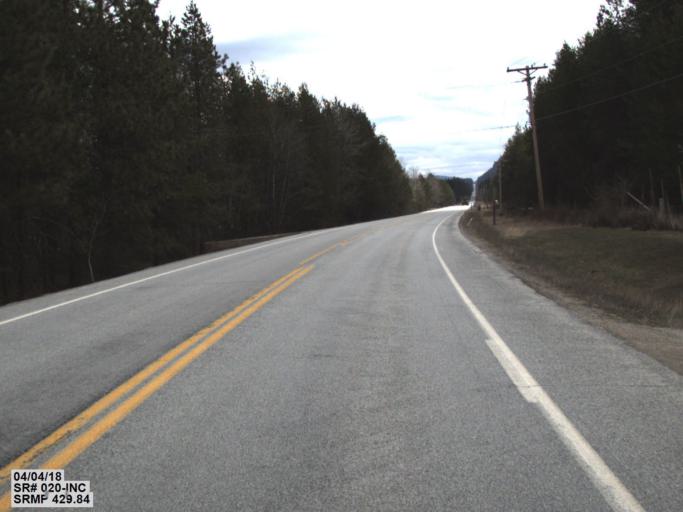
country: US
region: Washington
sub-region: Pend Oreille County
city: Newport
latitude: 48.2311
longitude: -117.1653
